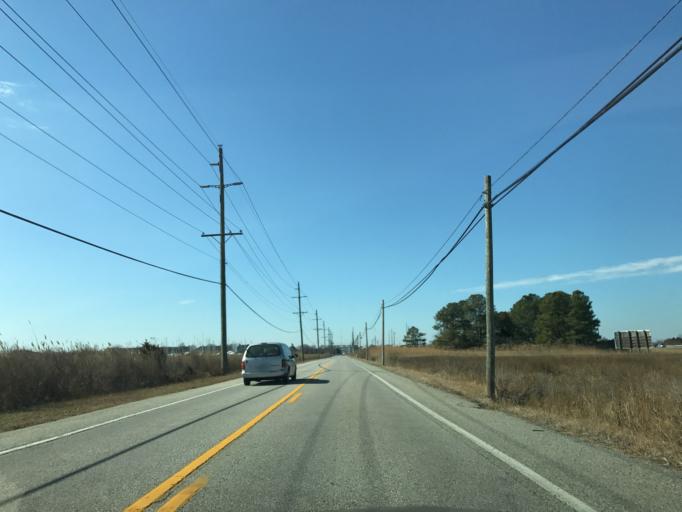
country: US
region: Maryland
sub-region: Queen Anne's County
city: Grasonville
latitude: 38.9655
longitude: -76.2281
